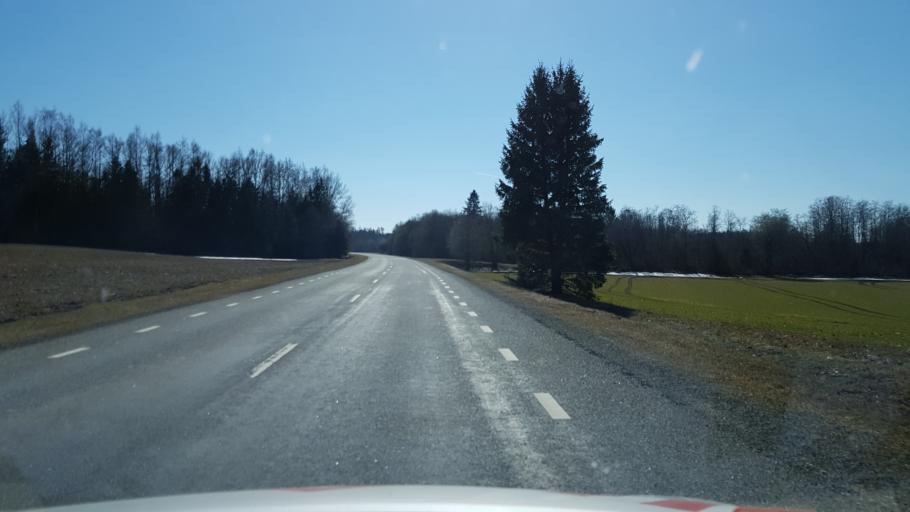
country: EE
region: Jaervamaa
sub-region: Jaerva-Jaani vald
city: Jarva-Jaani
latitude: 59.0979
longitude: 25.9825
